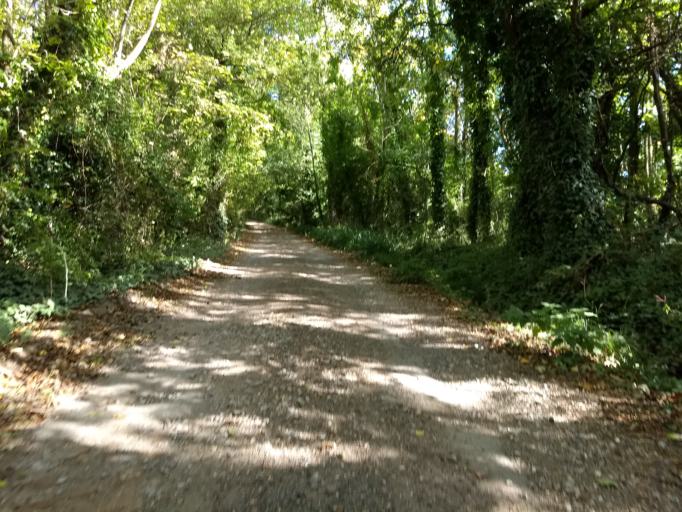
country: GB
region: England
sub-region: Isle of Wight
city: Brading
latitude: 50.7012
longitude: -1.1435
